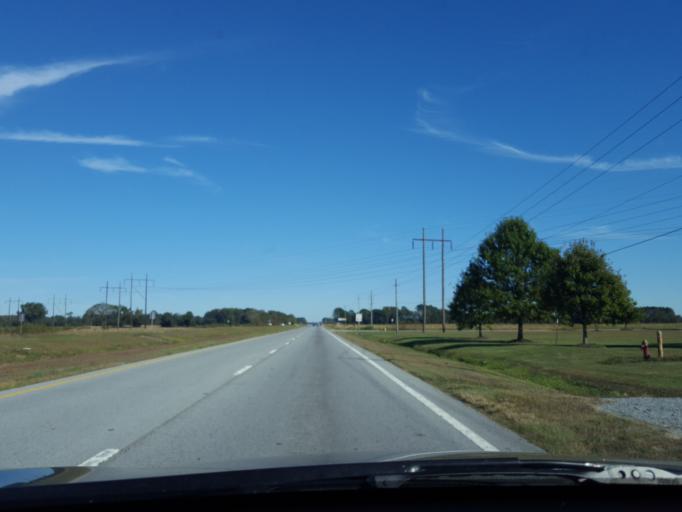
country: US
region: North Carolina
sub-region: Pitt County
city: Greenville
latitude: 35.6257
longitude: -77.3128
